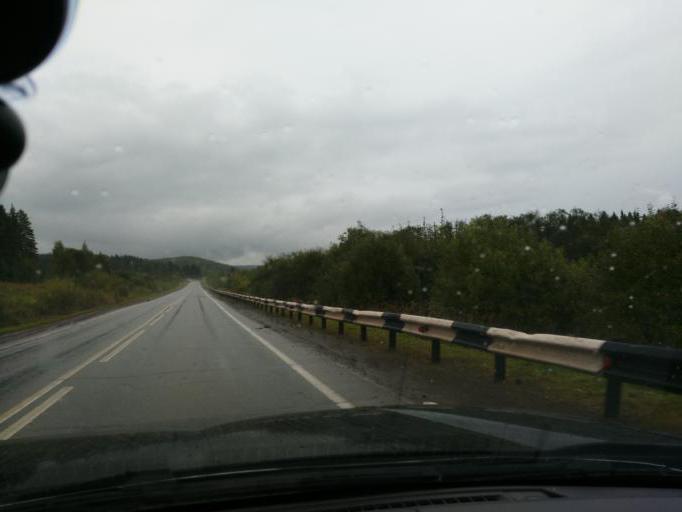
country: RU
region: Perm
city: Yugo-Kamskiy
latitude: 57.7240
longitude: 55.6773
